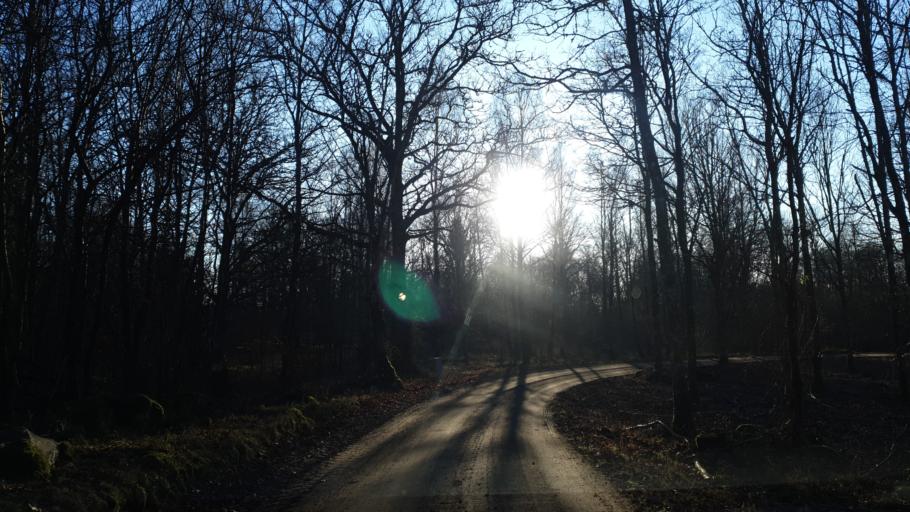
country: SE
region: Blekinge
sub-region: Karlskrona Kommun
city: Nattraby
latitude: 56.2550
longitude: 15.4087
